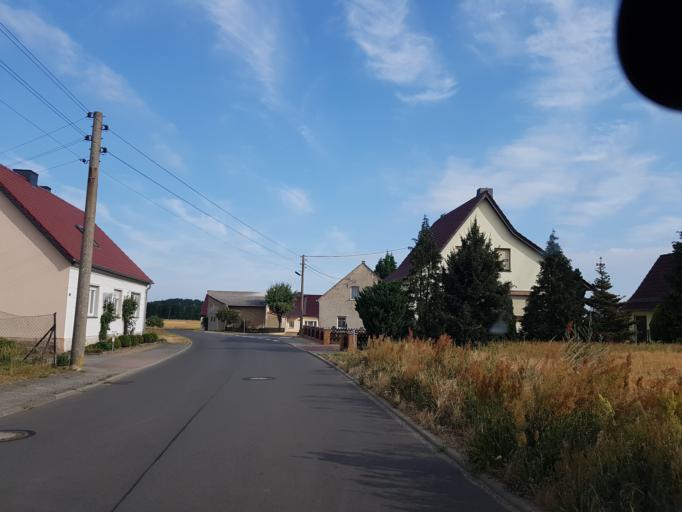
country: DE
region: Brandenburg
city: Luckau
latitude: 51.8411
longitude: 13.6374
